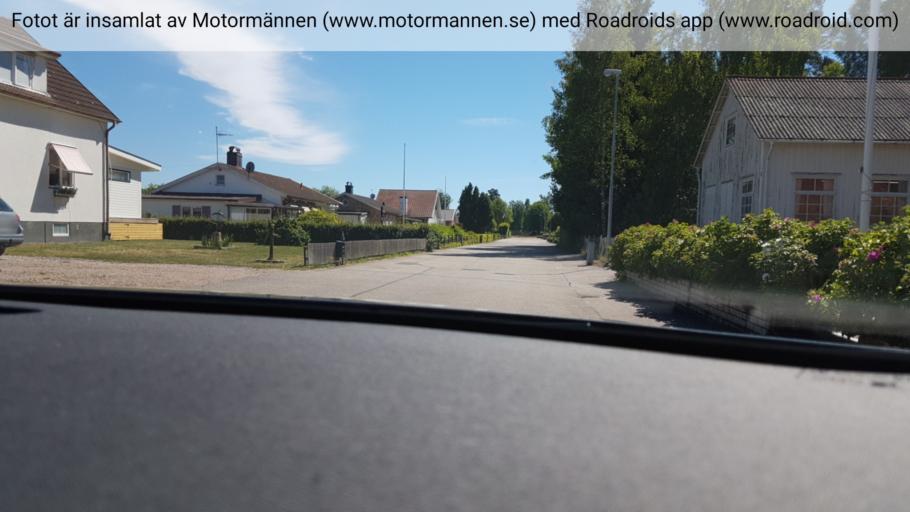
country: SE
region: Joenkoeping
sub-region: Gnosjo Kommun
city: Hillerstorp
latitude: 57.3117
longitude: 13.8802
